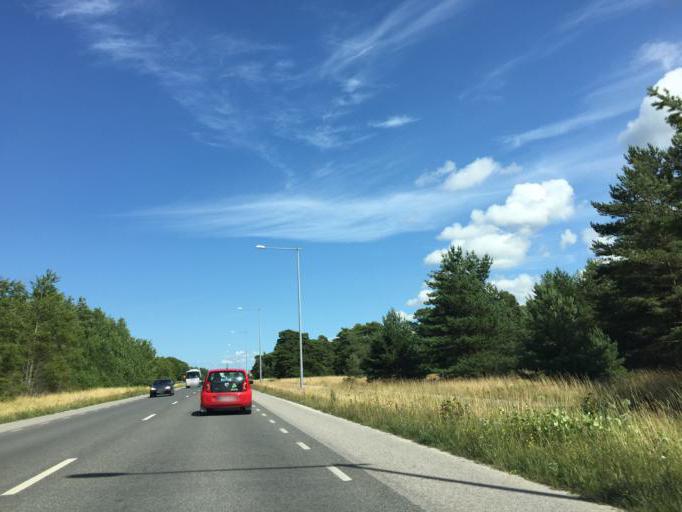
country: SE
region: Gotland
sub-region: Gotland
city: Vibble
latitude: 57.6161
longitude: 18.2674
